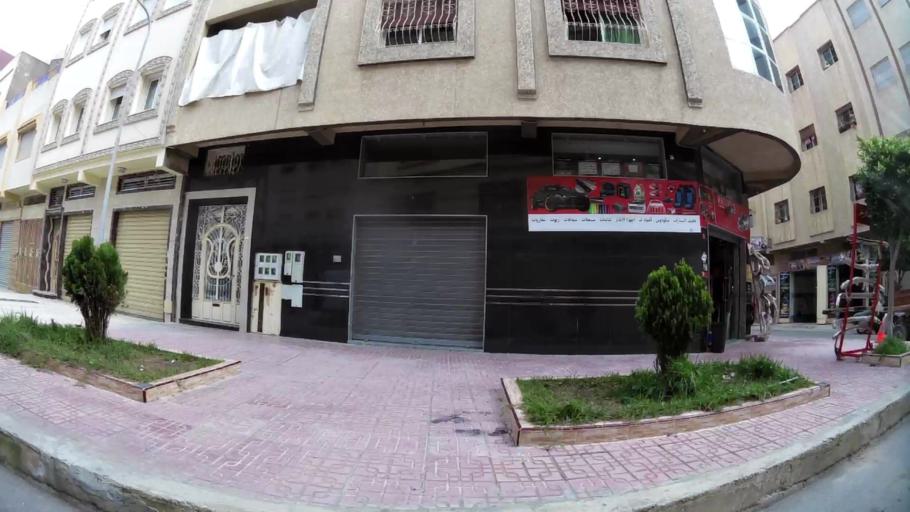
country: MA
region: Tanger-Tetouan
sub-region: Tanger-Assilah
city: Tangier
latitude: 35.7544
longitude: -5.7977
